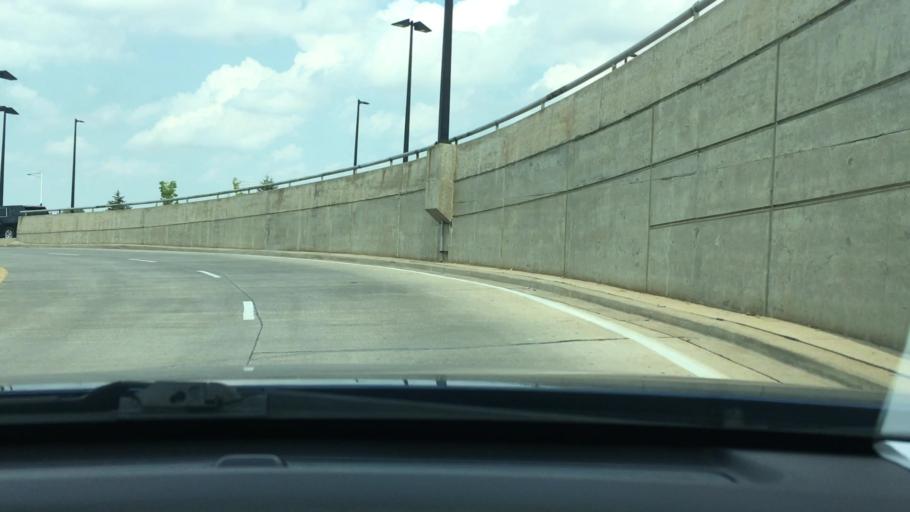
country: US
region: Illinois
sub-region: Cook County
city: Stickney
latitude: 41.7908
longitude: -87.7405
